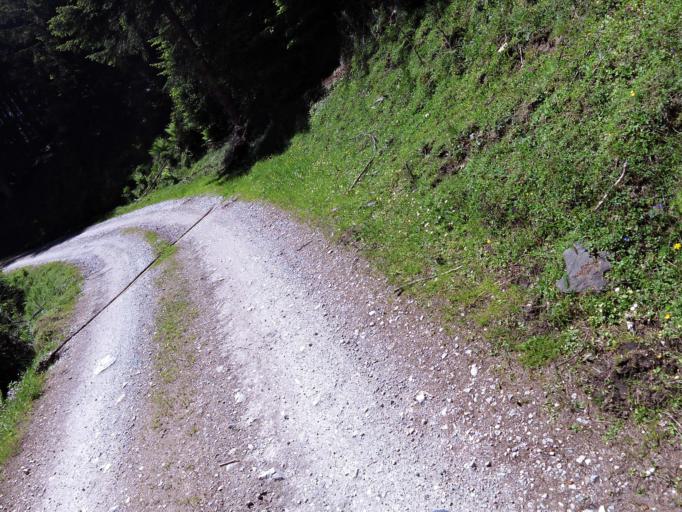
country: AT
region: Tyrol
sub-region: Politischer Bezirk Innsbruck Land
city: Neustift im Stubaital
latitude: 47.1152
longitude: 11.2913
